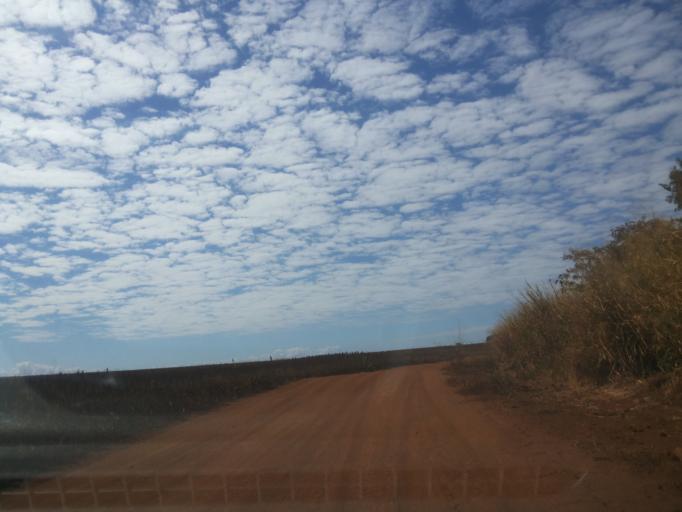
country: BR
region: Minas Gerais
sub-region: Centralina
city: Centralina
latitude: -18.5686
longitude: -49.2204
